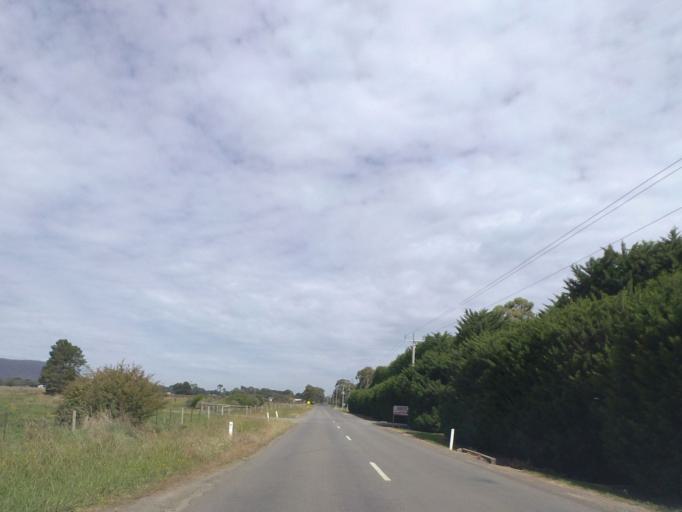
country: AU
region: Victoria
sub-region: Hume
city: Sunbury
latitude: -37.3238
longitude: 144.5417
